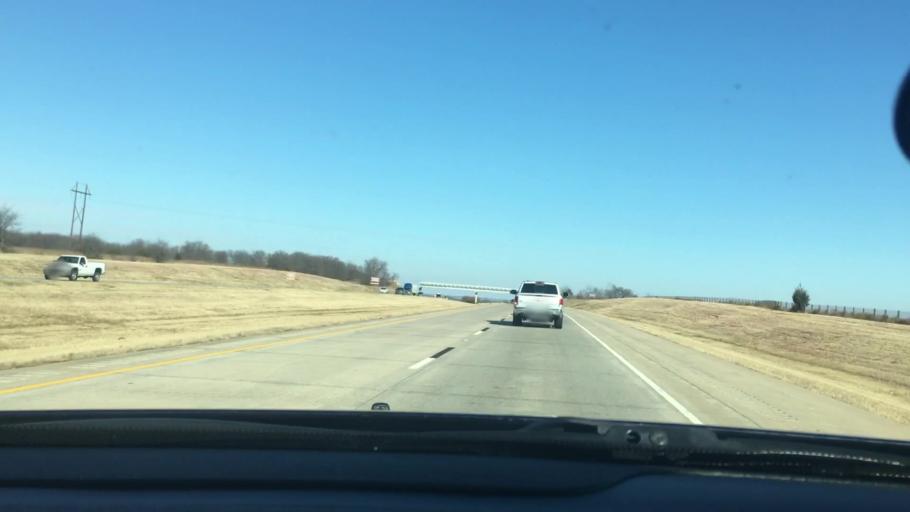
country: US
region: Oklahoma
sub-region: Love County
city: Marietta
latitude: 33.9584
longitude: -97.1340
